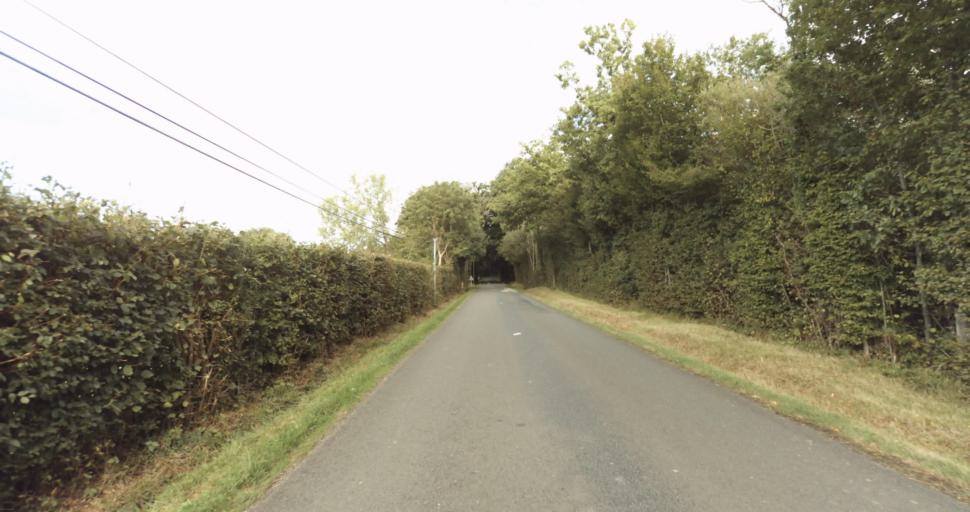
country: FR
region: Lower Normandy
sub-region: Departement de l'Orne
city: Gace
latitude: 48.8117
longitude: 0.2415
